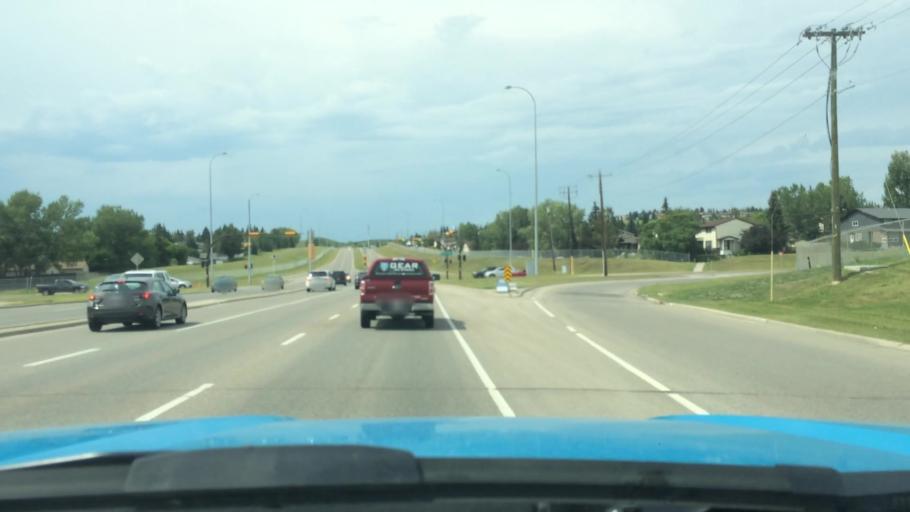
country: CA
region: Alberta
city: Calgary
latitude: 51.1147
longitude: -114.1531
